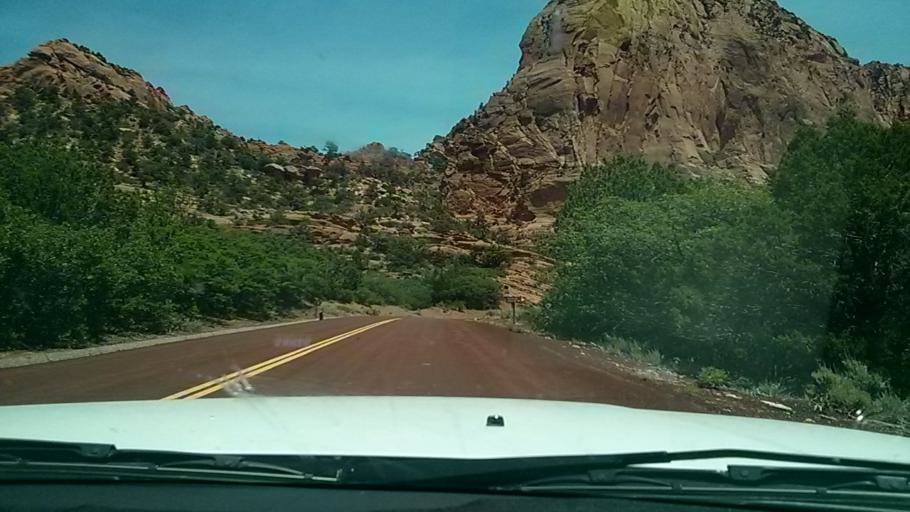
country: US
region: Utah
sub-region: Washington County
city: Toquerville
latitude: 37.4548
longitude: -113.1875
